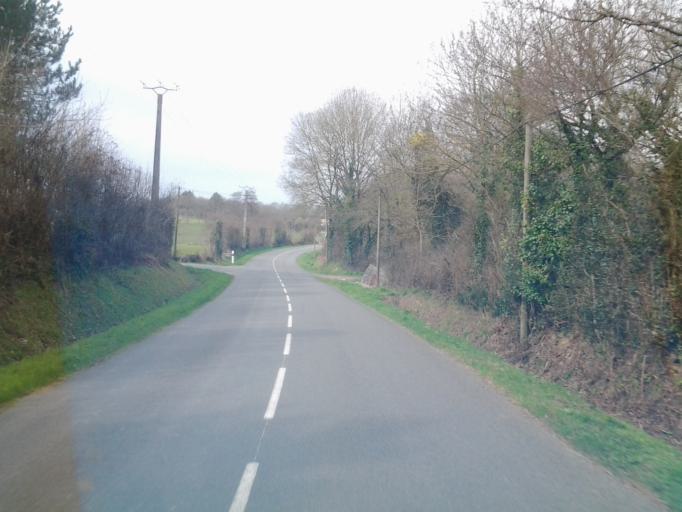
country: FR
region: Pays de la Loire
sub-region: Departement de la Vendee
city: Venansault
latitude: 46.6883
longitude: -1.5385
